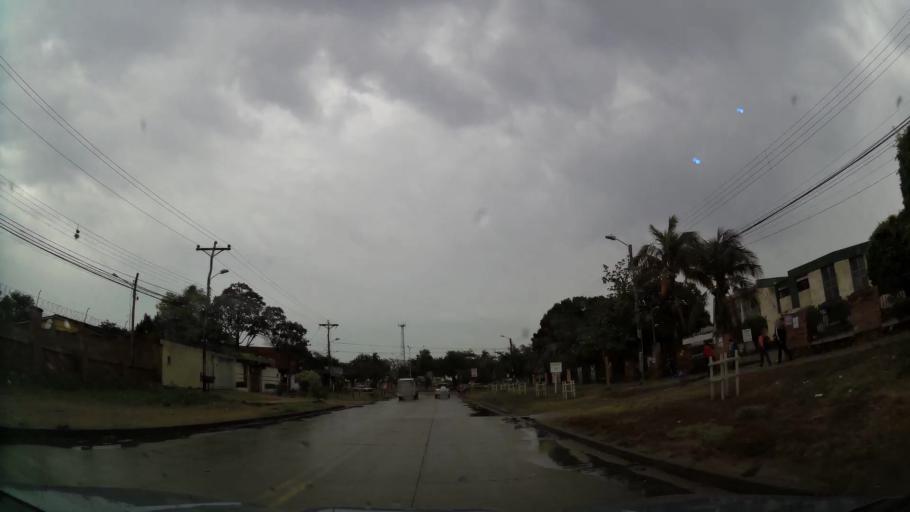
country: BO
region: Santa Cruz
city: Santa Cruz de la Sierra
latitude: -17.7814
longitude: -63.1442
